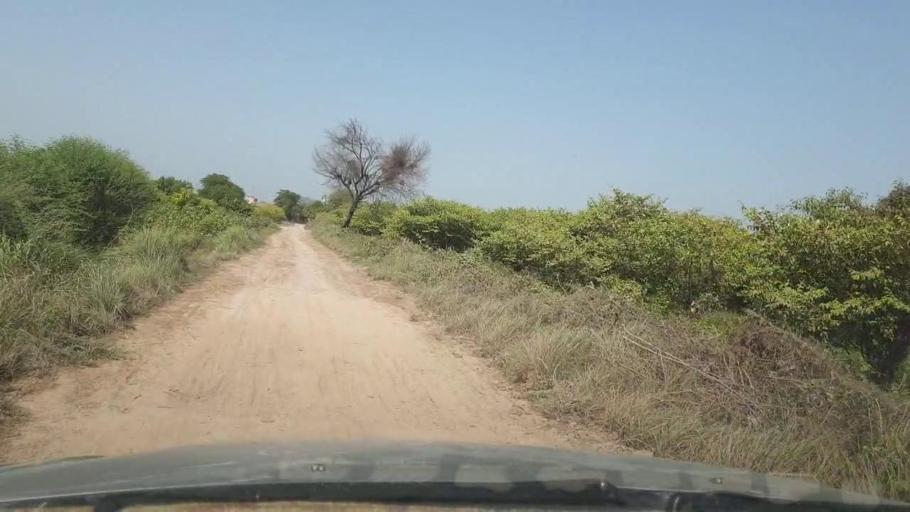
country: PK
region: Sindh
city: Tando Ghulam Ali
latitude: 25.1564
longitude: 68.9089
